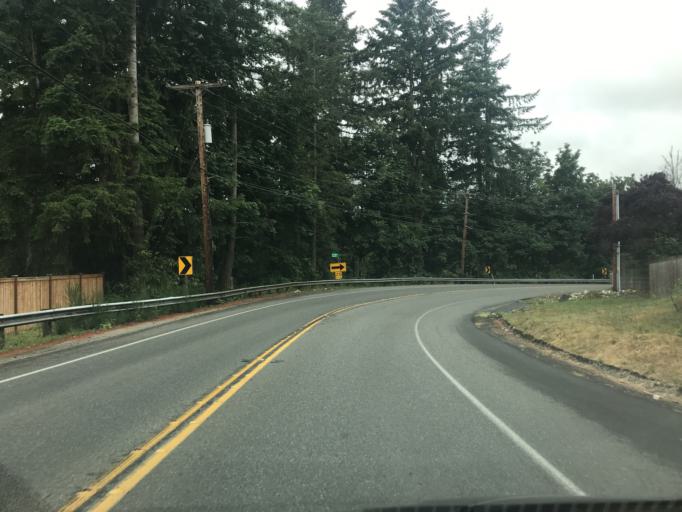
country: US
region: Washington
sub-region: King County
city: Lake Morton-Berrydale
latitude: 47.3420
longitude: -122.0984
